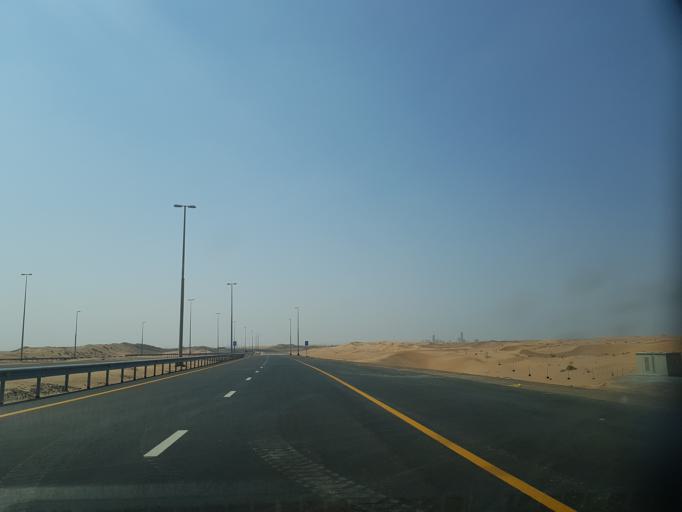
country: AE
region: Ash Shariqah
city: Adh Dhayd
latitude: 25.2679
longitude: 55.6567
